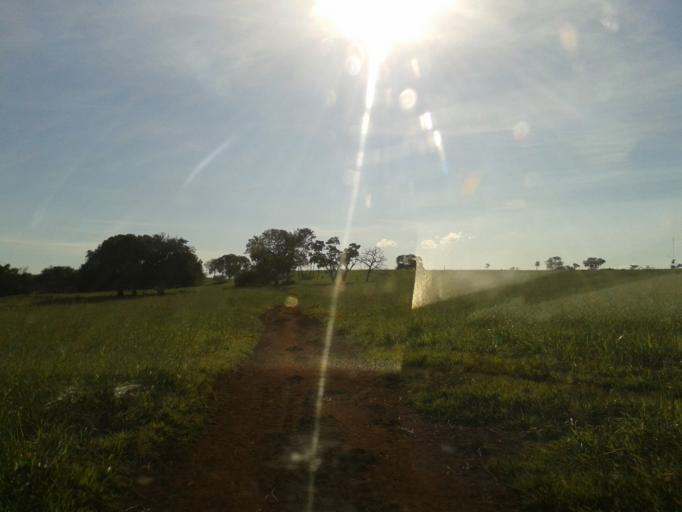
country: BR
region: Minas Gerais
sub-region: Santa Vitoria
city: Santa Vitoria
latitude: -18.9962
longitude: -50.3530
